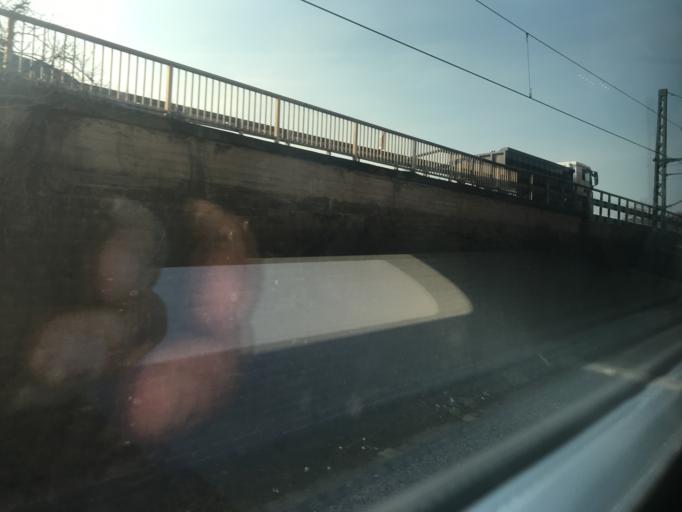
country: DE
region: Rheinland-Pfalz
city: Wasserliesch
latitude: 49.7106
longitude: 6.5427
